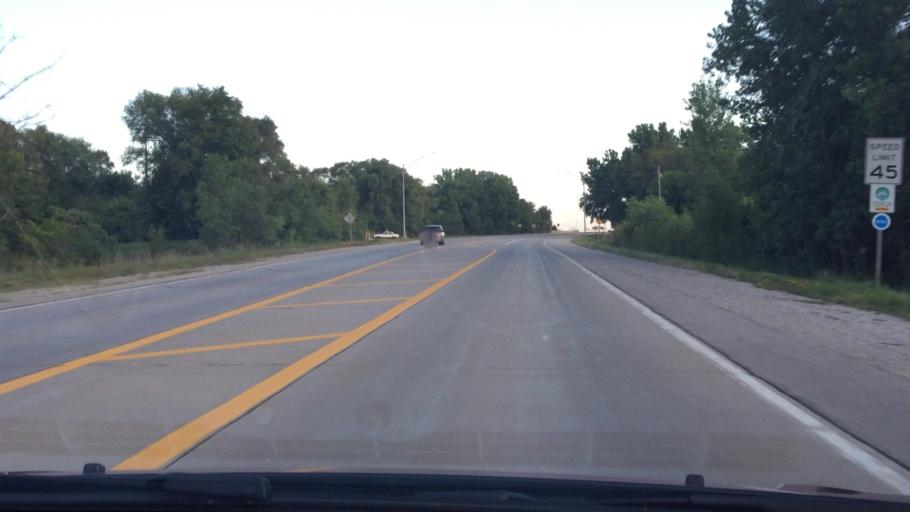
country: US
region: Iowa
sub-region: Muscatine County
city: Muscatine
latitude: 41.4594
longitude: -91.0312
